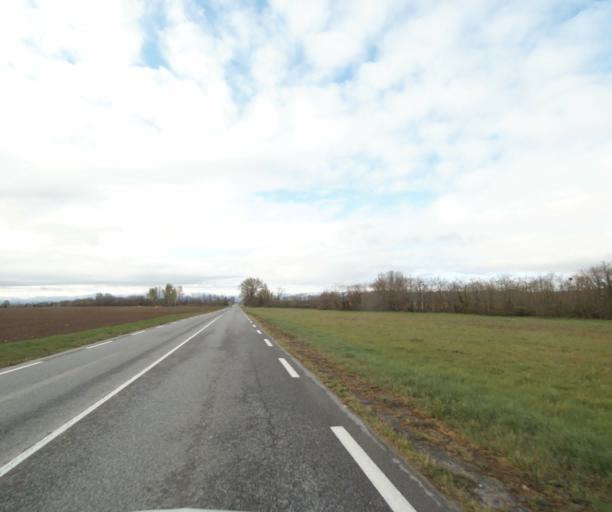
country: FR
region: Midi-Pyrenees
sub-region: Departement de l'Ariege
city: Saverdun
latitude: 43.2224
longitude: 1.6066
